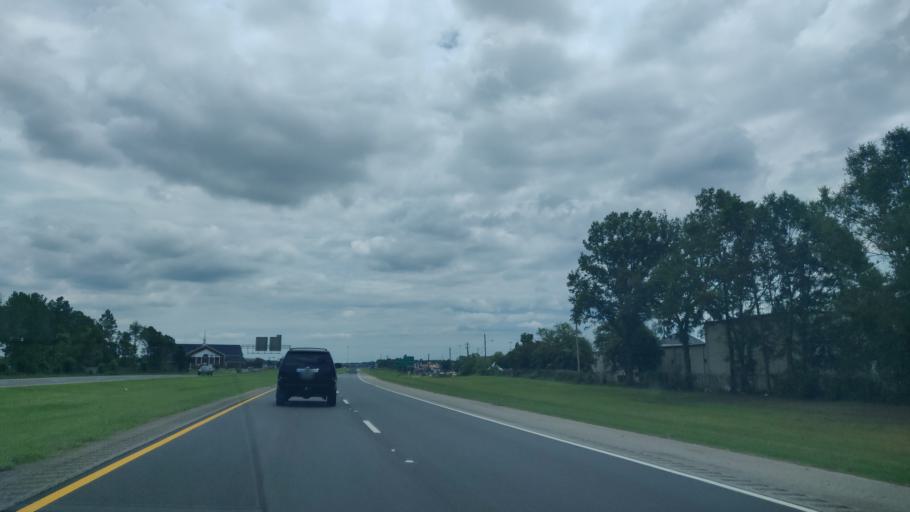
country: US
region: Georgia
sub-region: Dougherty County
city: Albany
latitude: 31.6223
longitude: -84.2213
